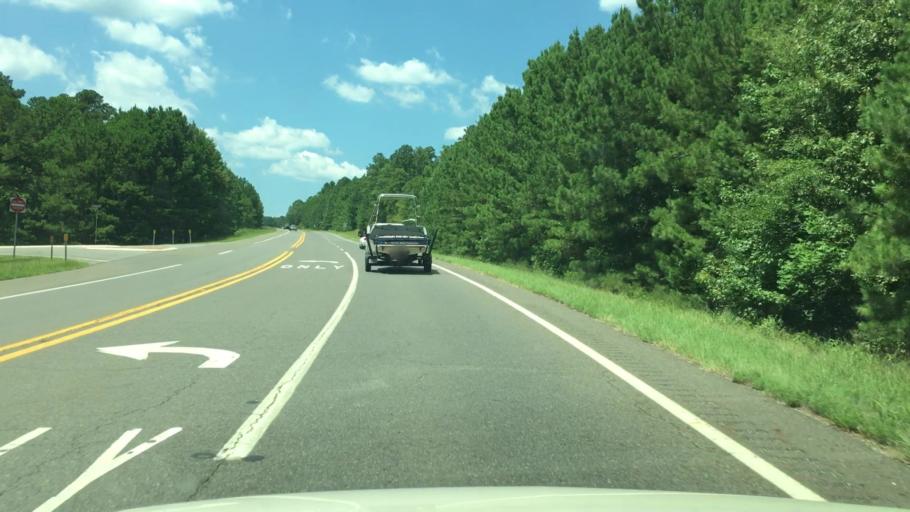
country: US
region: Arkansas
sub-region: Clark County
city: Arkadelphia
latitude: 34.2100
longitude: -93.0800
